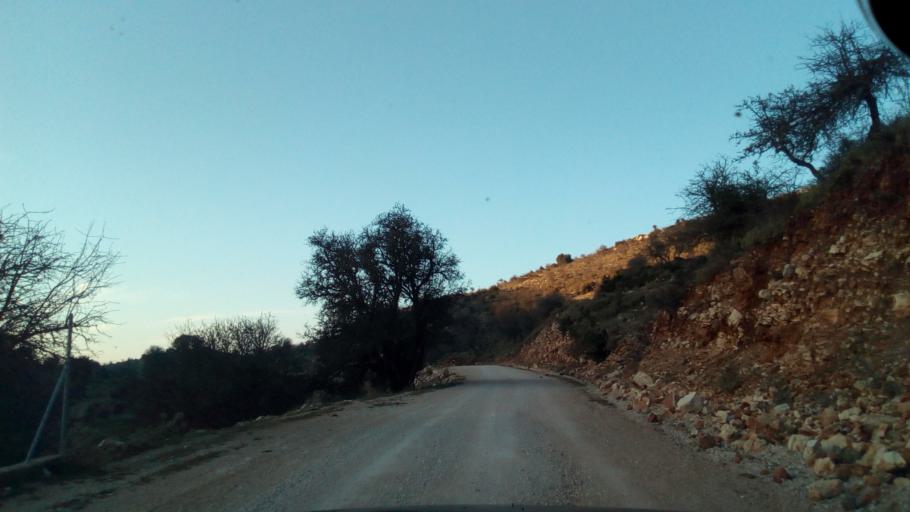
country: GR
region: West Greece
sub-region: Nomos Aitolias kai Akarnanias
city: Nafpaktos
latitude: 38.4589
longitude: 21.8384
